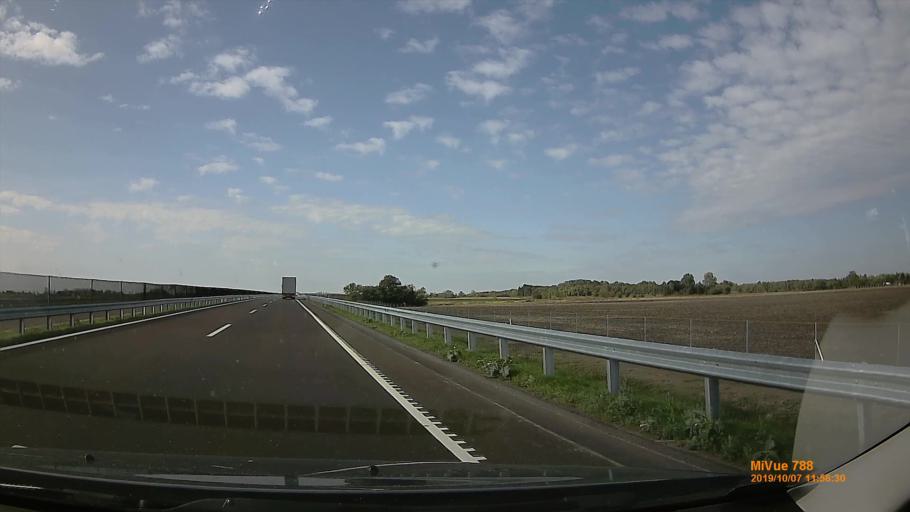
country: HU
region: Bekes
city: Szarvas
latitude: 46.8176
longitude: 20.5516
